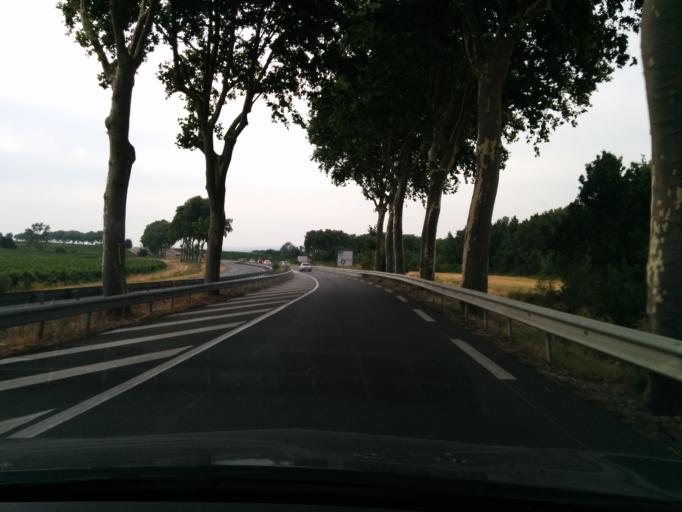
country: FR
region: Languedoc-Roussillon
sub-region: Departement de l'Aude
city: Pennautier
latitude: 43.2367
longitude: 2.3179
